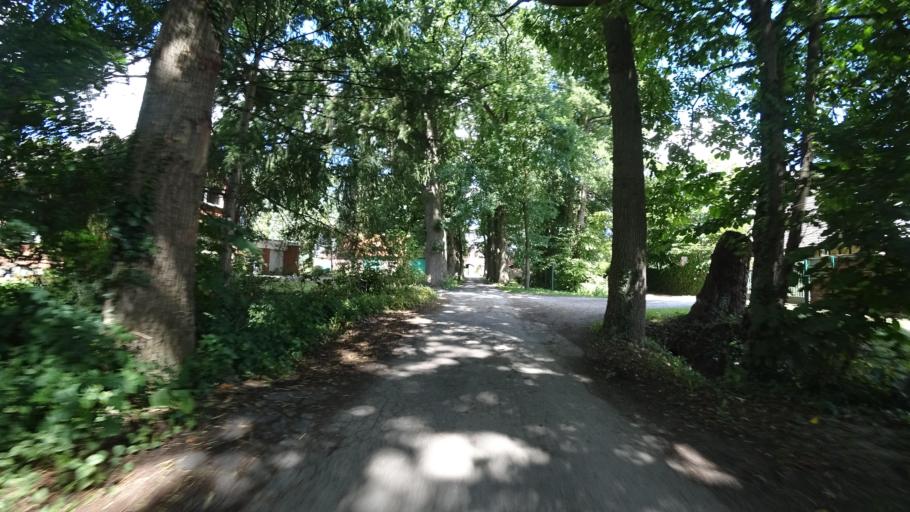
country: DE
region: North Rhine-Westphalia
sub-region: Regierungsbezirk Detmold
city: Guetersloh
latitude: 51.9387
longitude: 8.3910
